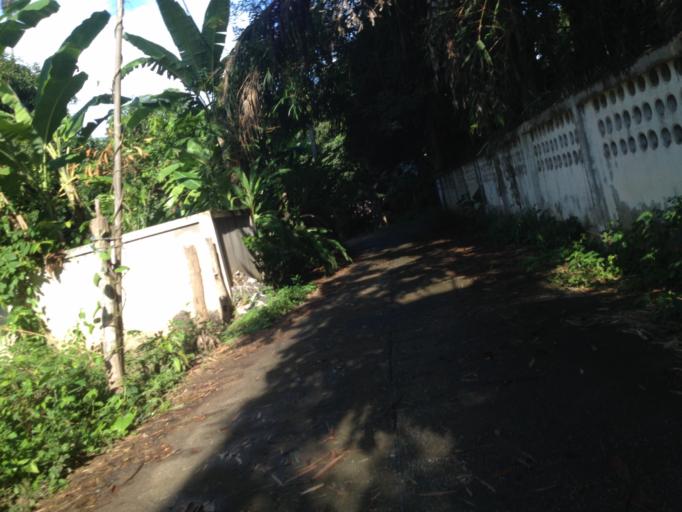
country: TH
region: Chiang Mai
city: Hang Dong
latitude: 18.7030
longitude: 98.9194
